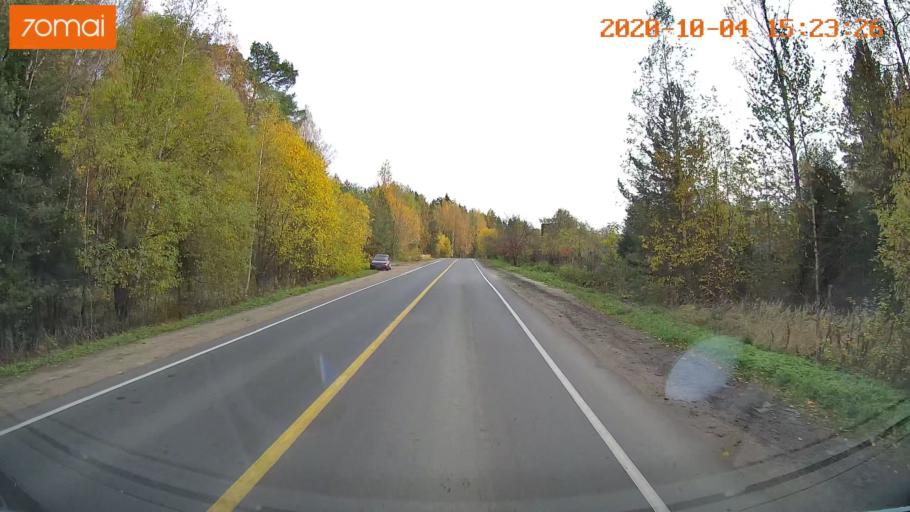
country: RU
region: Ivanovo
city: Bogorodskoye
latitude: 57.0736
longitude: 40.9491
